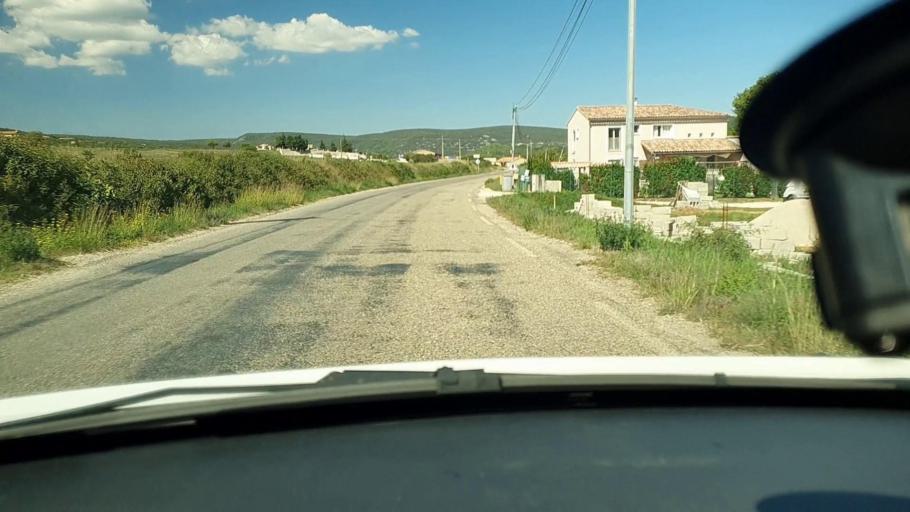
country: FR
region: Languedoc-Roussillon
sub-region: Departement du Gard
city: Goudargues
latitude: 44.1648
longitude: 4.4547
